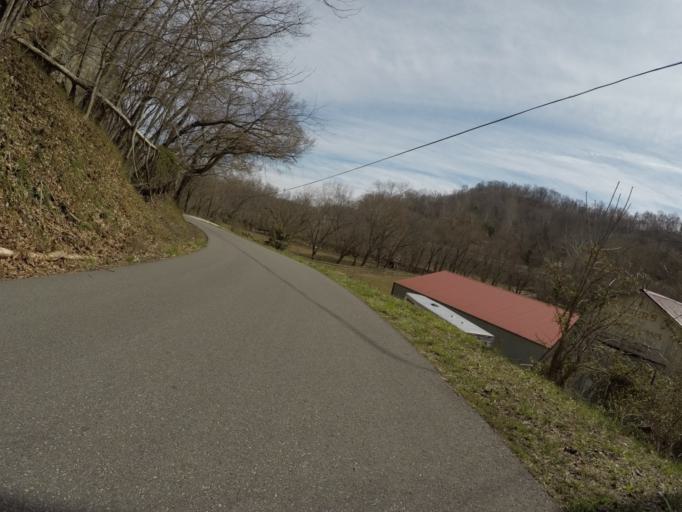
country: US
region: West Virginia
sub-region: Wayne County
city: Ceredo
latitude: 38.3735
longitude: -82.5511
